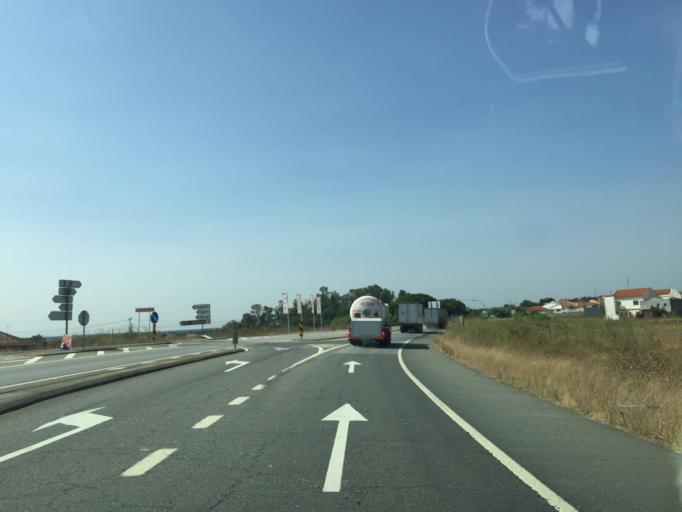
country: PT
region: Beja
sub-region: Aljustrel
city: Aljustrel
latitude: 37.9429
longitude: -8.3790
